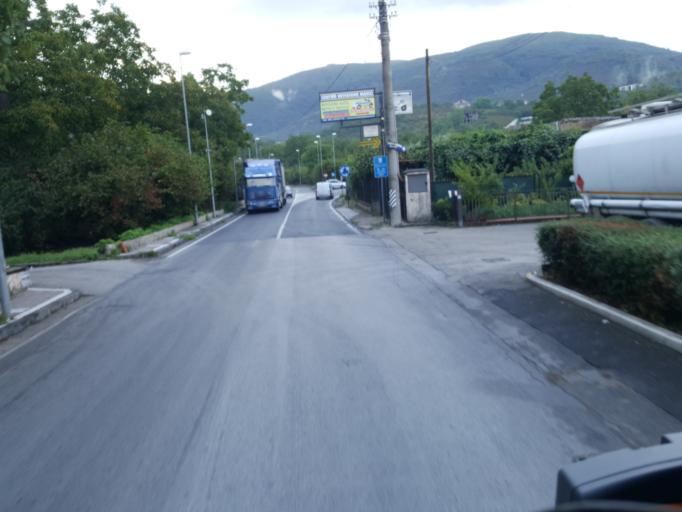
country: IT
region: Campania
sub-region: Provincia di Napoli
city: Palma Campania
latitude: 40.8781
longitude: 14.5592
